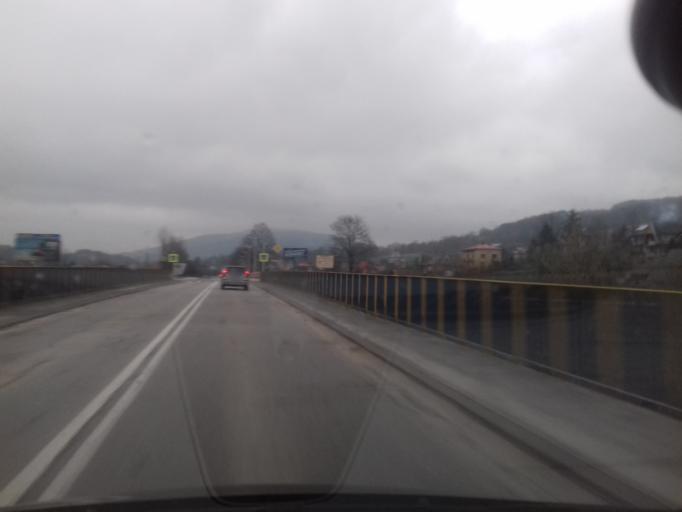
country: PL
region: Lesser Poland Voivodeship
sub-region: Powiat limanowski
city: Mszana Dolna
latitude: 49.6857
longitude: 20.0507
